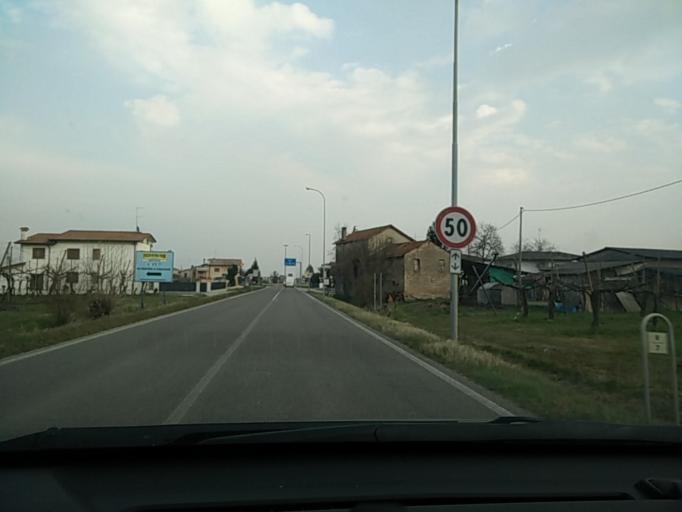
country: IT
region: Veneto
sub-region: Provincia di Treviso
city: Codogne
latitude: 45.8614
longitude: 12.4093
